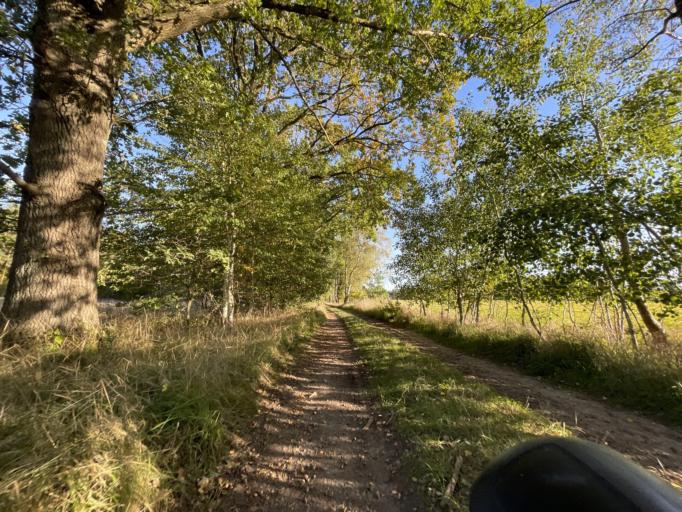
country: DE
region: Lower Saxony
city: Vastorf
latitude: 53.1963
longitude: 10.5246
